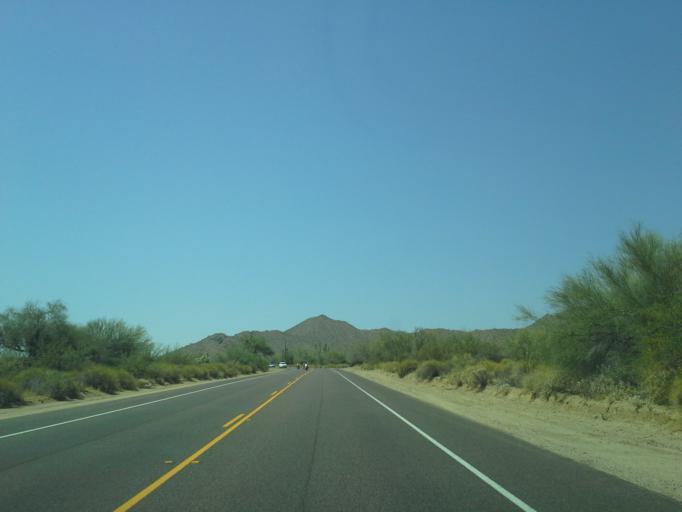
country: US
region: Arizona
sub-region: Pinal County
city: Apache Junction
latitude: 33.5212
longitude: -111.6172
